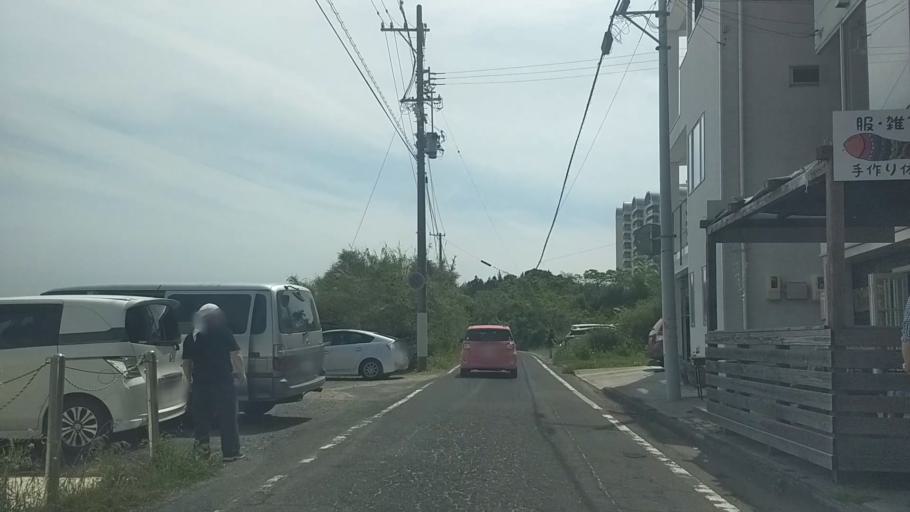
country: JP
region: Shizuoka
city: Kosai-shi
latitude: 34.7786
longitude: 137.5697
